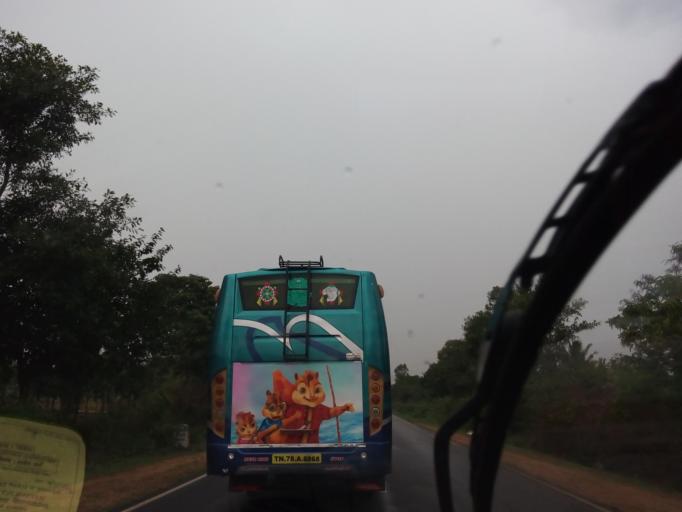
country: IN
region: Karnataka
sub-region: Hassan
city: Hassan
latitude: 13.1152
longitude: 76.0071
